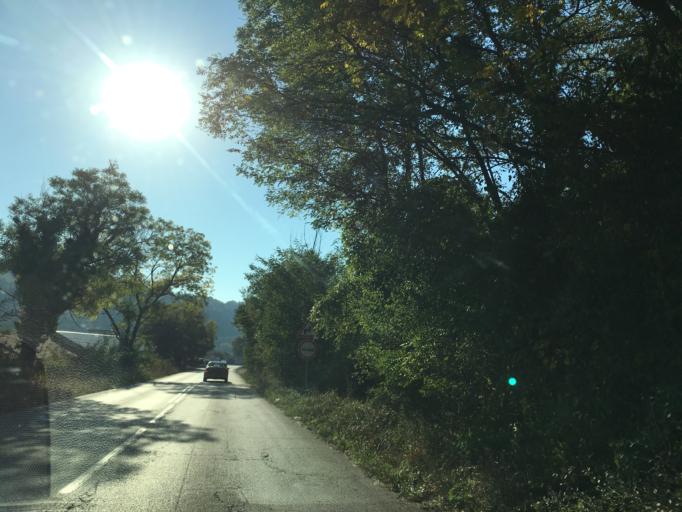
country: BG
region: Pazardzhik
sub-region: Obshtina Belovo
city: Belovo
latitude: 42.2427
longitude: 23.9425
